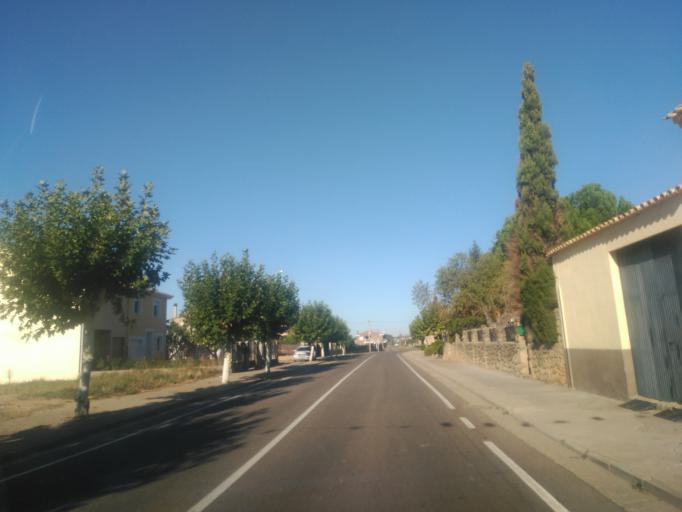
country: ES
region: Castille and Leon
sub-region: Provincia de Burgos
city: Zazuar
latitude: 41.6951
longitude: -3.5580
